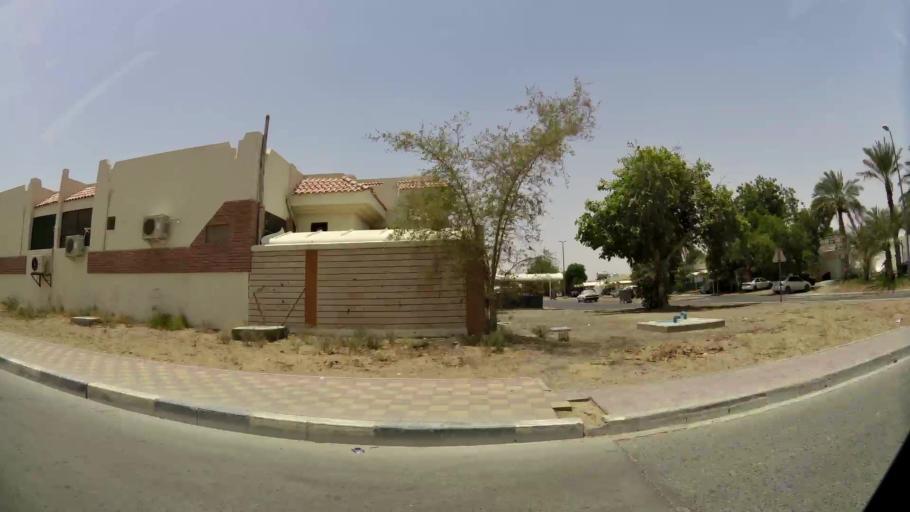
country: AE
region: Abu Dhabi
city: Al Ain
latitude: 24.2054
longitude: 55.7785
